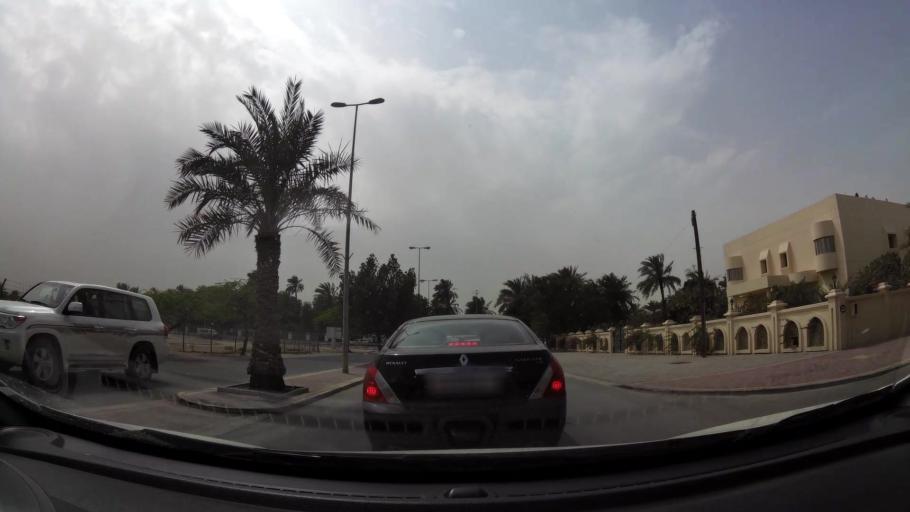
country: BH
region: Northern
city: Ar Rifa'
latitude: 26.1199
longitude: 50.5376
